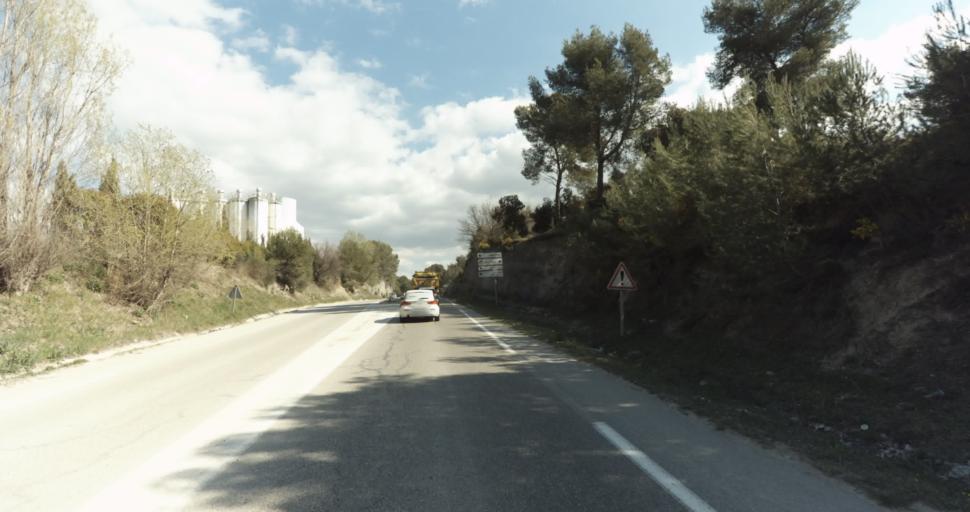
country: FR
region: Provence-Alpes-Cote d'Azur
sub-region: Departement des Bouches-du-Rhone
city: Gardanne
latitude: 43.4526
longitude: 5.4939
